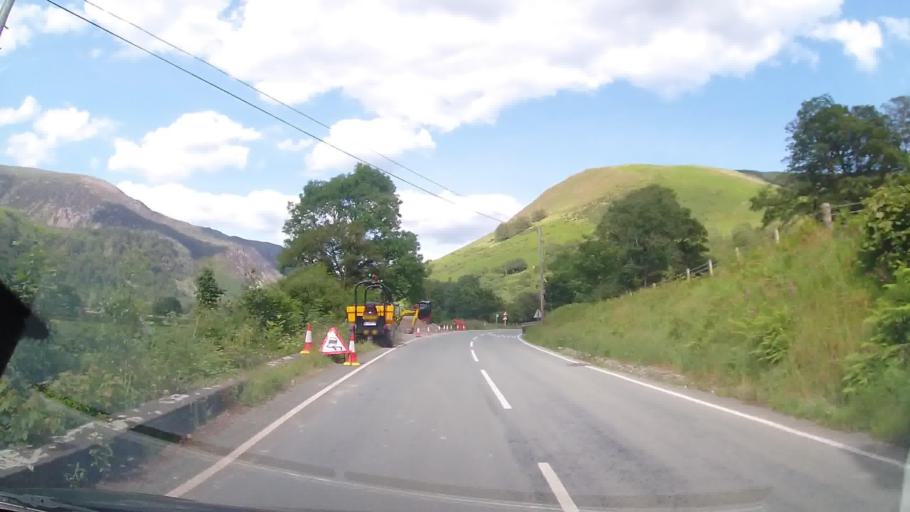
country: GB
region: Wales
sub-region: Gwynedd
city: Corris
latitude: 52.6763
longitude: -3.8846
